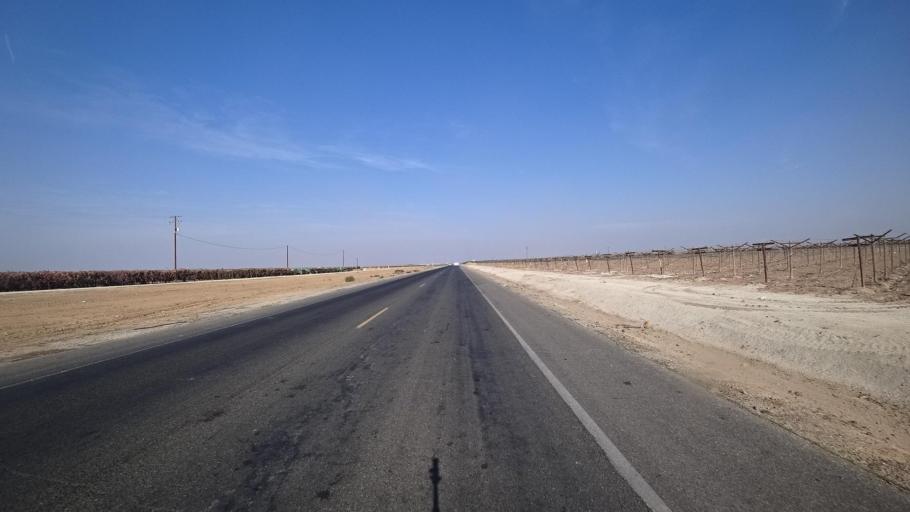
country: US
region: California
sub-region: Kern County
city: McFarland
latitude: 35.7232
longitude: -119.1564
